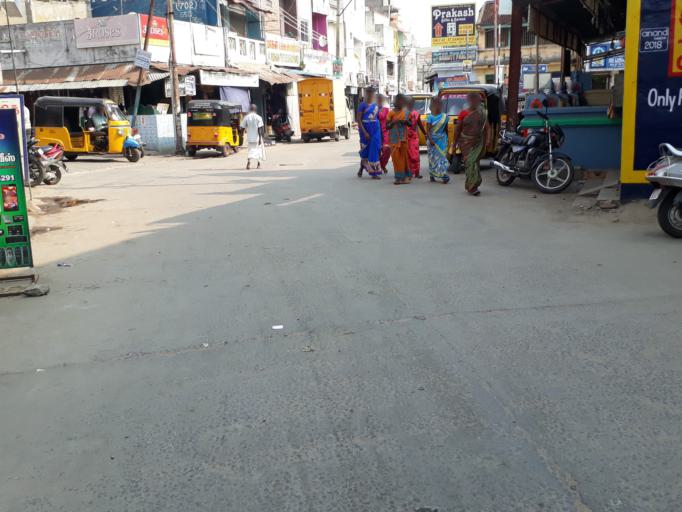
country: IN
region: Tamil Nadu
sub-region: Kancheepuram
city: Kanchipuram
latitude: 12.8322
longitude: 79.7074
